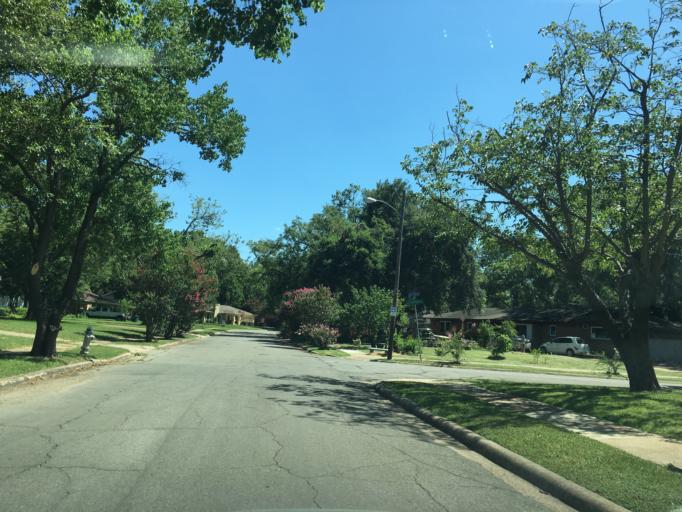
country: US
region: Texas
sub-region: Dallas County
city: Highland Park
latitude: 32.8387
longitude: -96.6985
